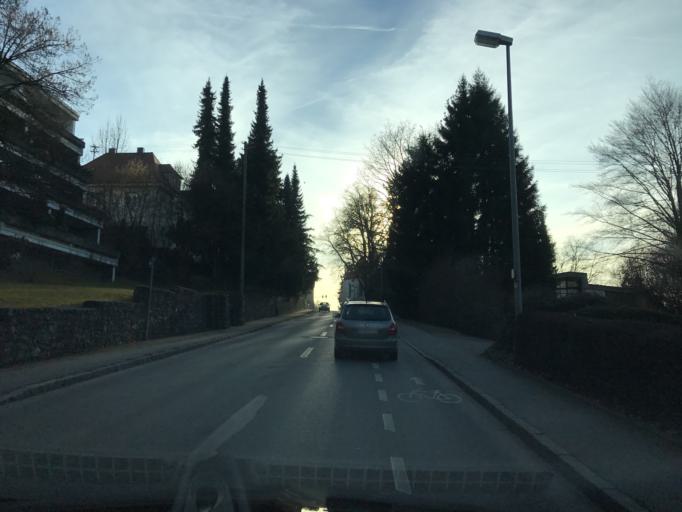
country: DE
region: Baden-Wuerttemberg
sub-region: Tuebingen Region
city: Bad Waldsee
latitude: 47.9175
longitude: 9.7514
